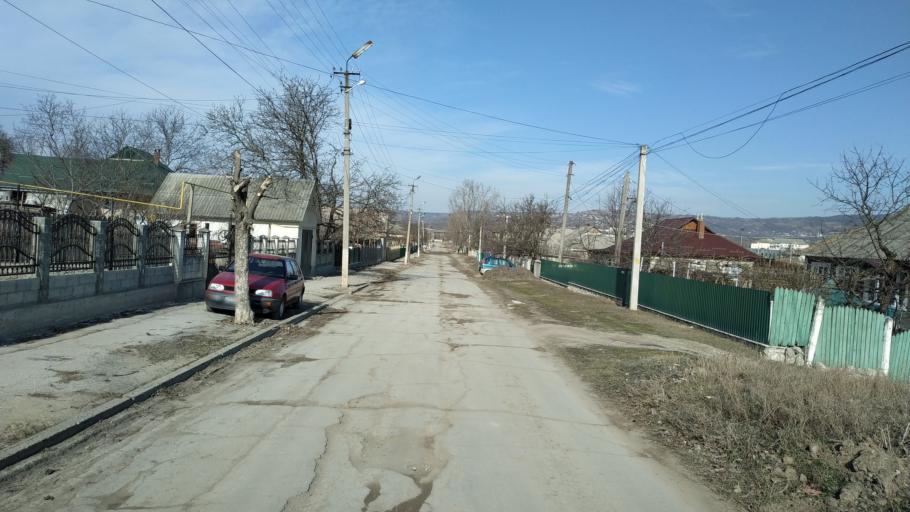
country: MD
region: Nisporeni
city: Nisporeni
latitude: 47.0684
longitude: 28.1740
